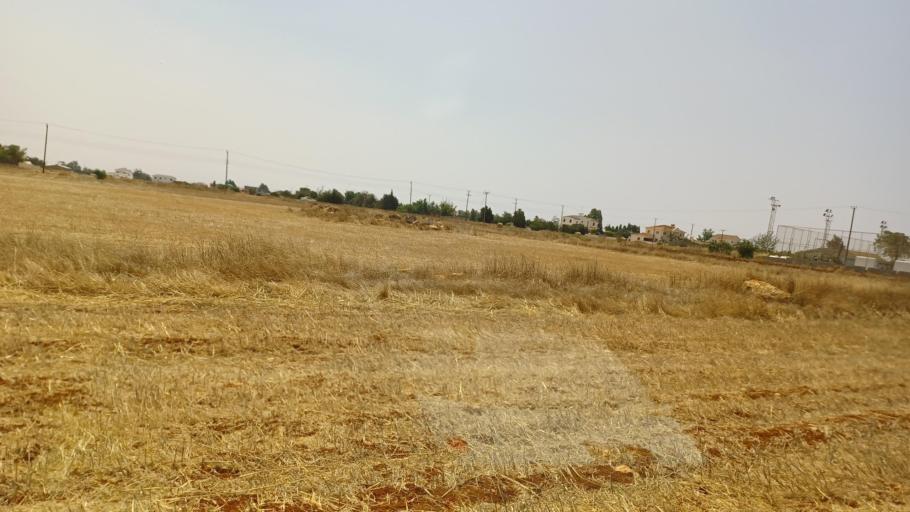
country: CY
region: Ammochostos
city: Liopetri
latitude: 34.9892
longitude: 33.8517
